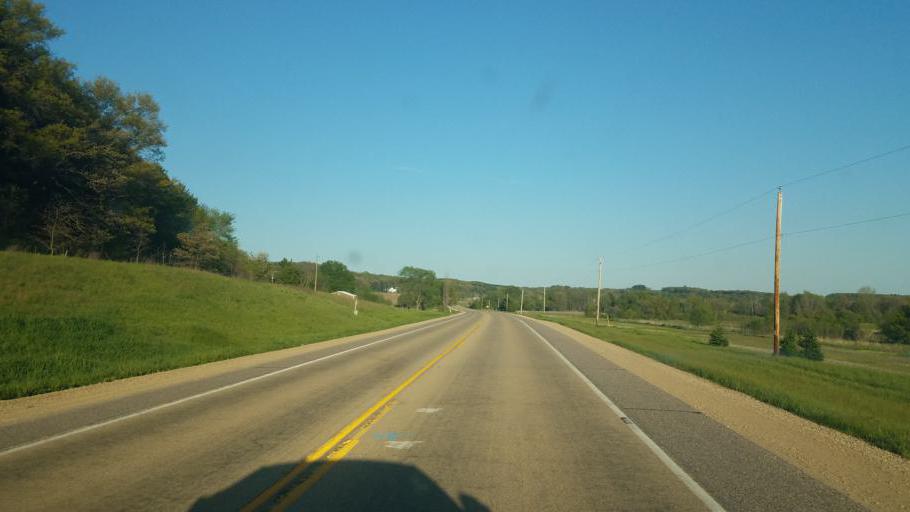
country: US
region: Wisconsin
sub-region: Juneau County
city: Elroy
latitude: 43.6203
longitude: -90.1565
